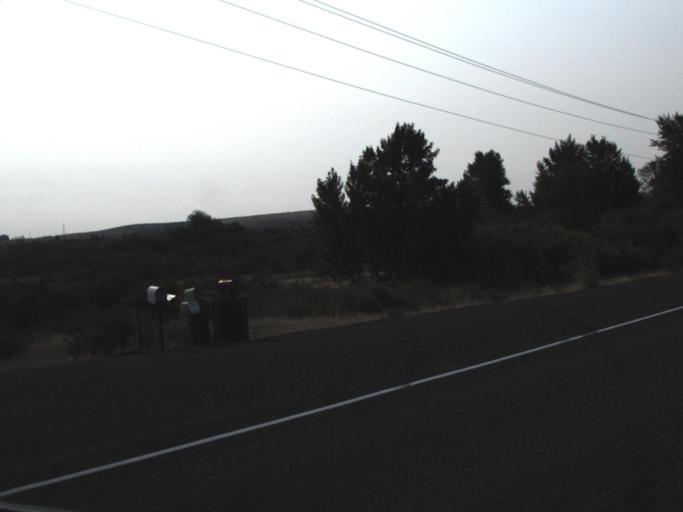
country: US
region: Washington
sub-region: Kittitas County
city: Ellensburg
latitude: 47.1075
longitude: -120.6641
